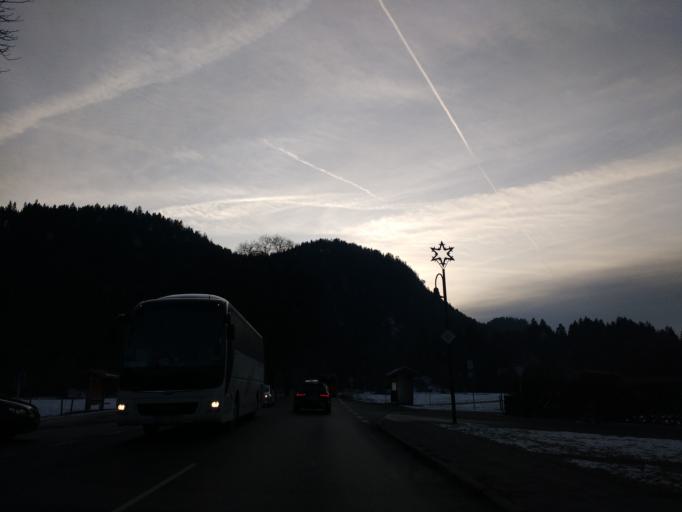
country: DE
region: Bavaria
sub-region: Swabia
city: Schwangau
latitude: 47.5677
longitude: 10.7201
